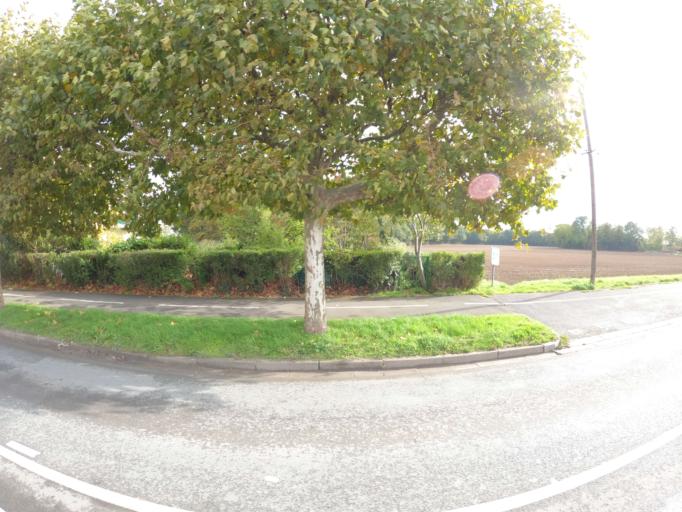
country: FR
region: Ile-de-France
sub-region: Departement de Seine-Saint-Denis
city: Montfermeil
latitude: 48.8968
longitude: 2.5907
